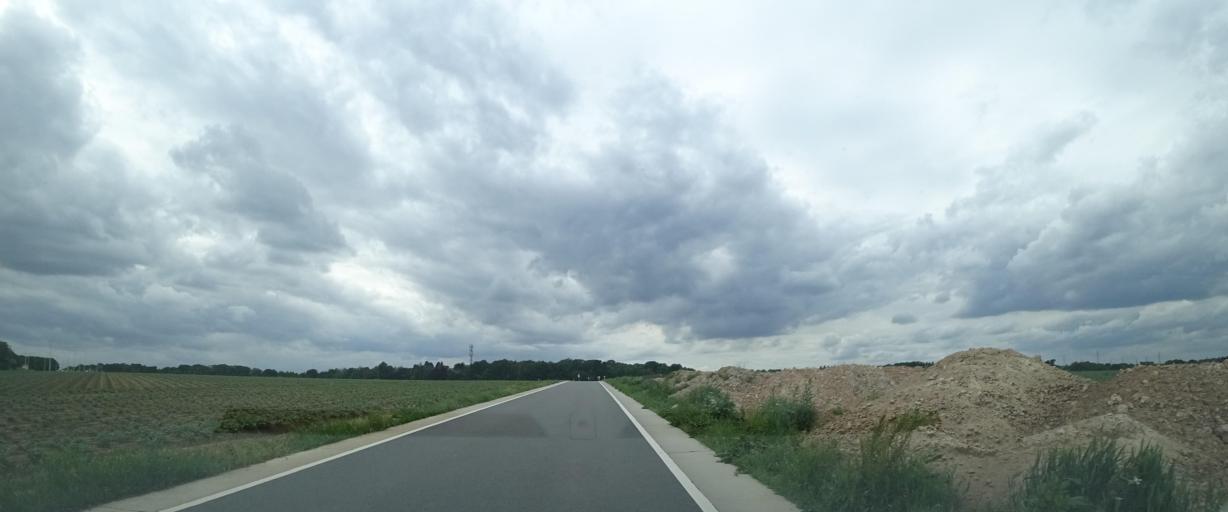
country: BE
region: Wallonia
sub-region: Province du Brabant Wallon
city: Court-Saint-Etienne
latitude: 50.6324
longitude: 4.5524
